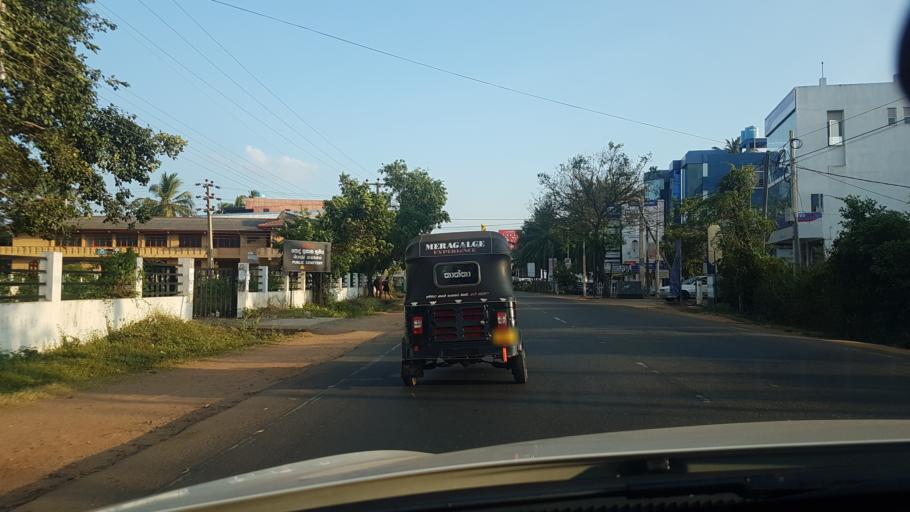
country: LK
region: North Western
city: Chilaw
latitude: 7.5703
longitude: 79.7982
